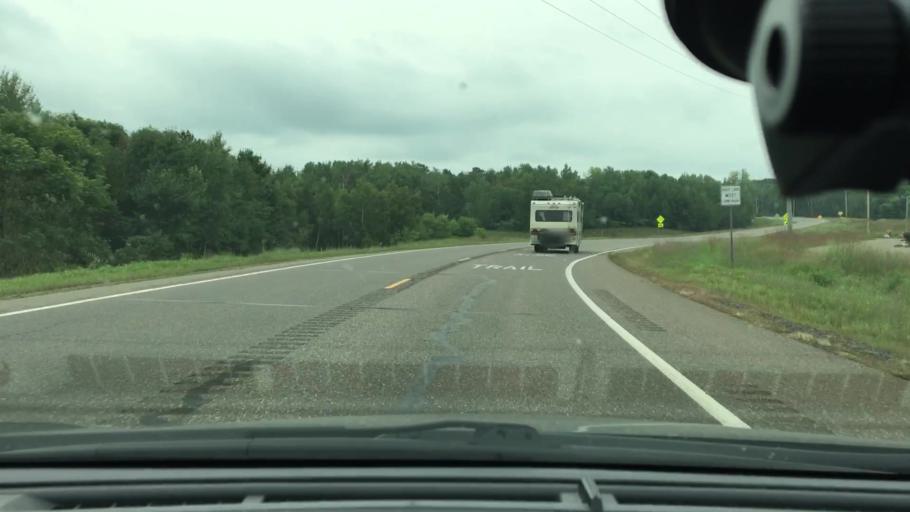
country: US
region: Minnesota
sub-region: Crow Wing County
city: Crosby
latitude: 46.4926
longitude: -93.9558
